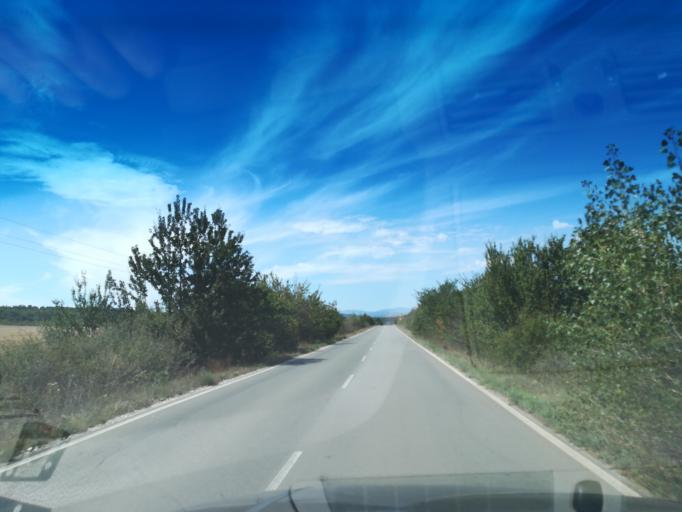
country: BG
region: Plovdiv
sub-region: Obshtina Suedinenie
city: Suedinenie
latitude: 42.4048
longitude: 24.5286
